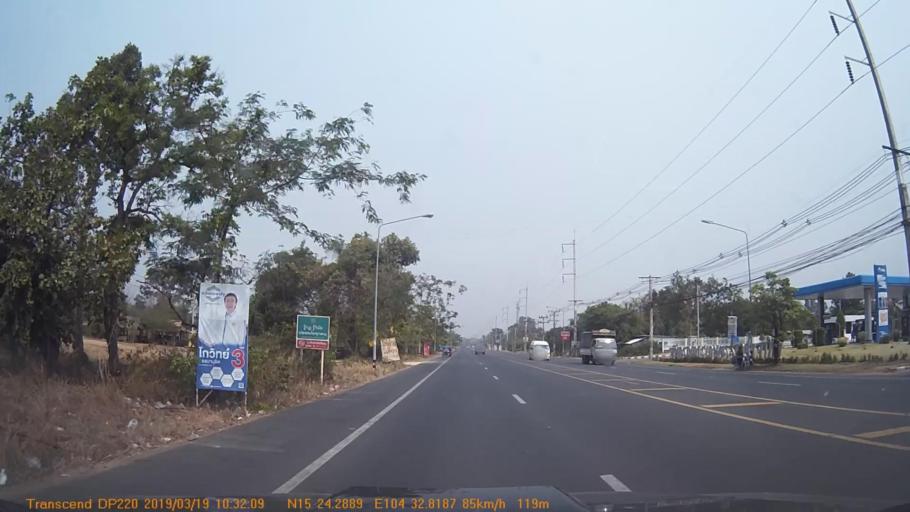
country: TH
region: Changwat Ubon Ratchathani
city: Khueang Nai
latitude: 15.4052
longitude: 104.5468
